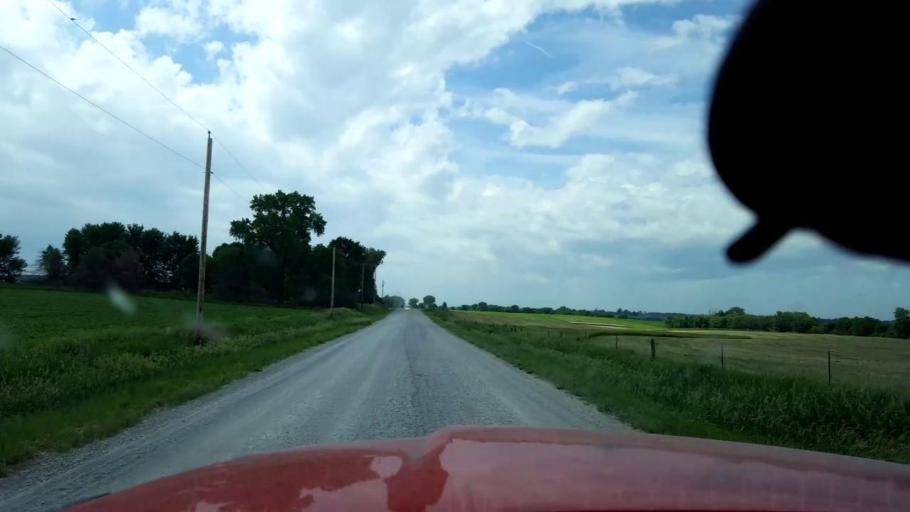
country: US
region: Iowa
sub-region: Cherokee County
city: Cherokee
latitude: 42.8194
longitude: -95.5346
